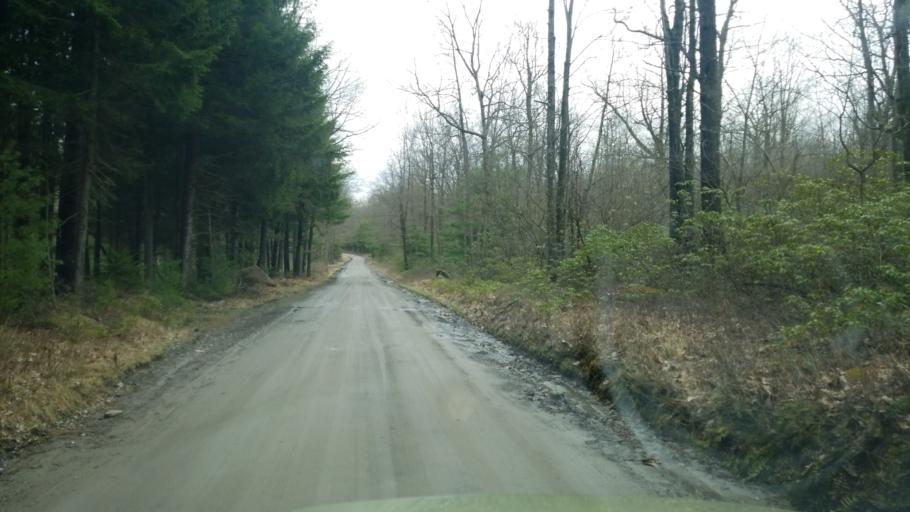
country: US
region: Pennsylvania
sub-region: Clearfield County
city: Shiloh
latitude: 41.1670
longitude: -78.2554
